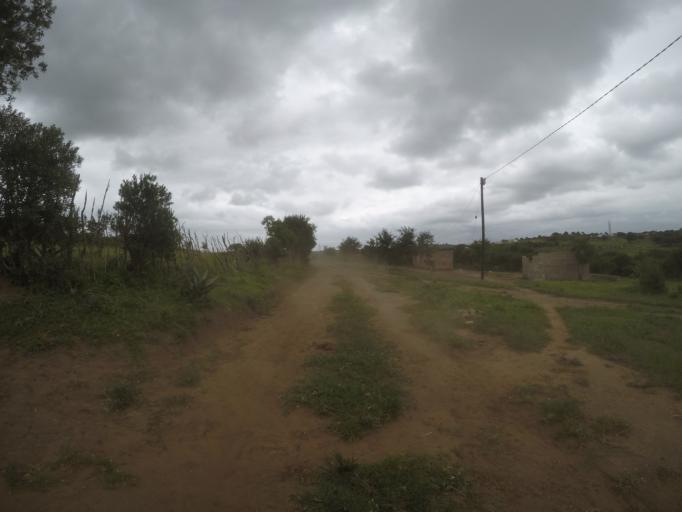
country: ZA
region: KwaZulu-Natal
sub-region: uThungulu District Municipality
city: Empangeni
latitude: -28.5925
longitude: 31.8432
